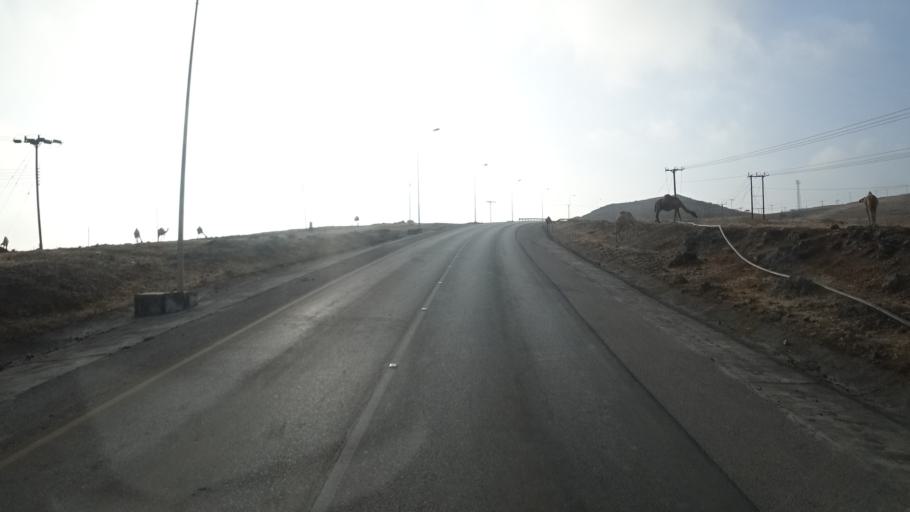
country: OM
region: Zufar
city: Salalah
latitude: 17.1197
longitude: 53.9805
